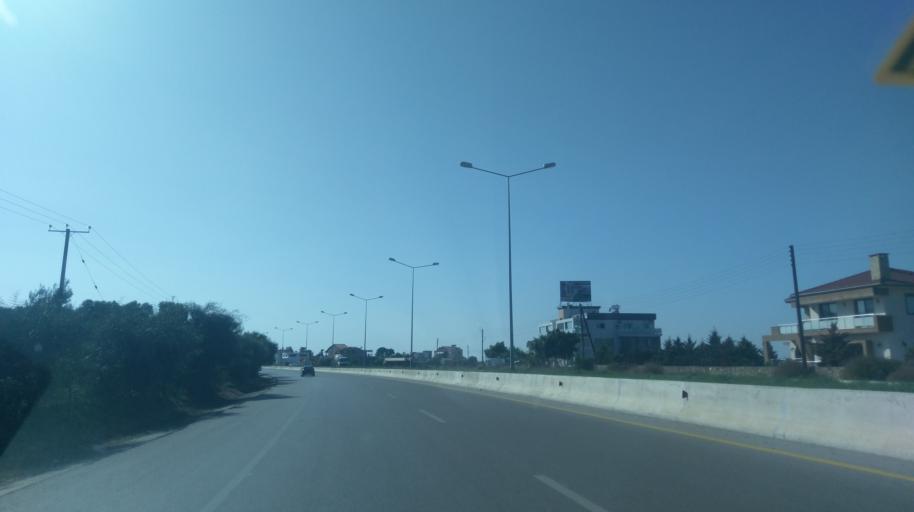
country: CY
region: Ammochostos
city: Trikomo
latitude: 35.2252
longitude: 33.8952
